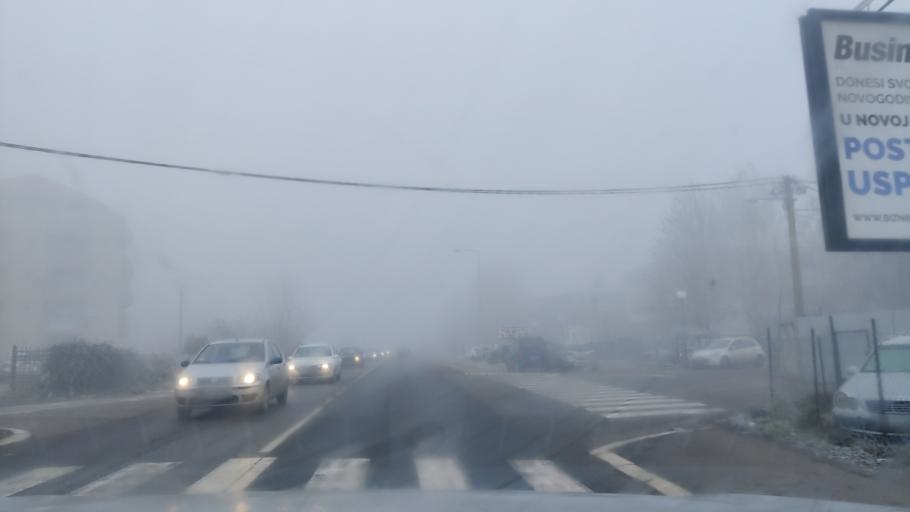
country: RS
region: Central Serbia
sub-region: Belgrade
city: Stari Grad
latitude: 44.8829
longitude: 20.4639
